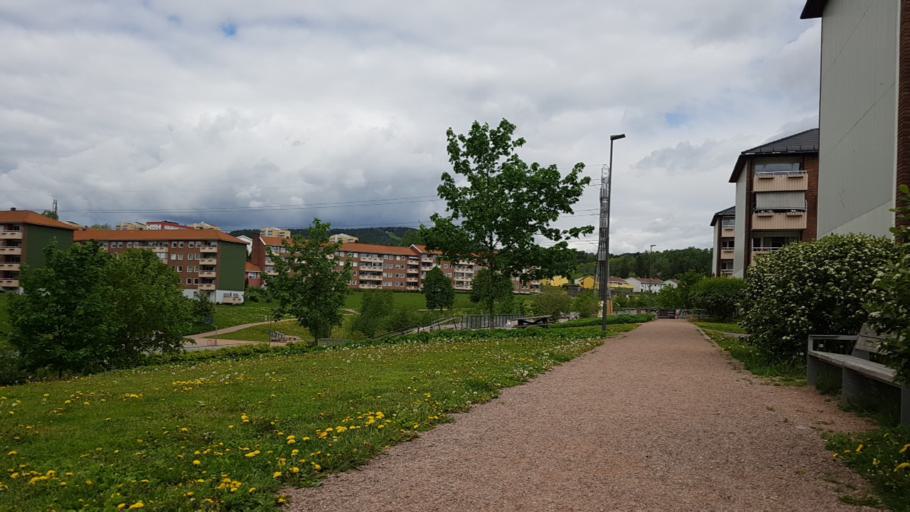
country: NO
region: Oslo
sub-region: Oslo
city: Oslo
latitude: 59.9381
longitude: 10.8225
